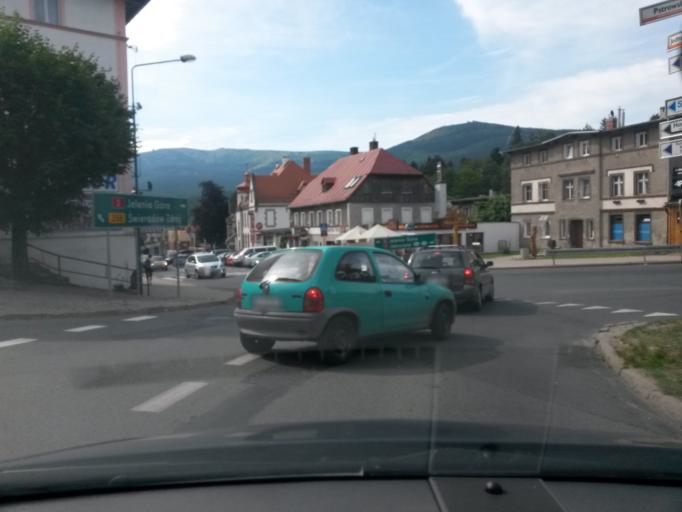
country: PL
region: Lower Silesian Voivodeship
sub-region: Powiat jeleniogorski
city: Szklarska Poreba
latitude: 50.8299
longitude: 15.5180
